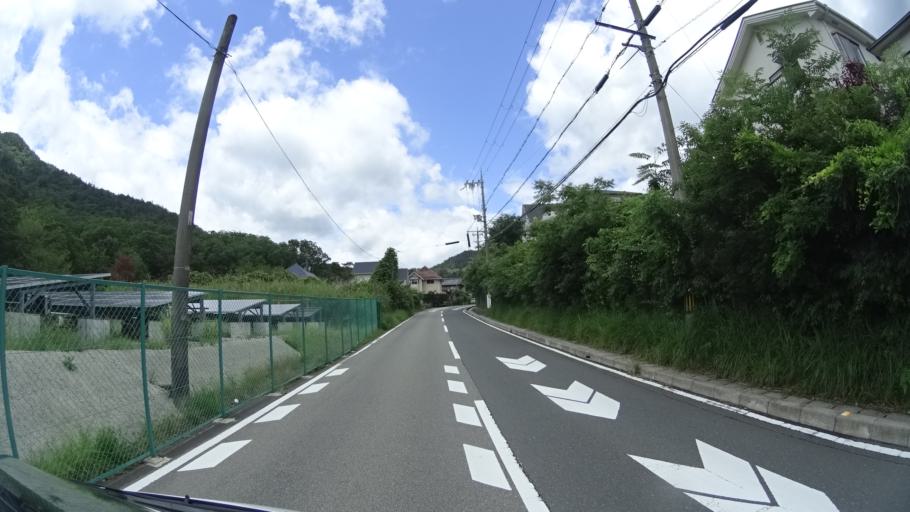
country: JP
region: Kyoto
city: Kameoka
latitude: 35.0150
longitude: 135.4249
